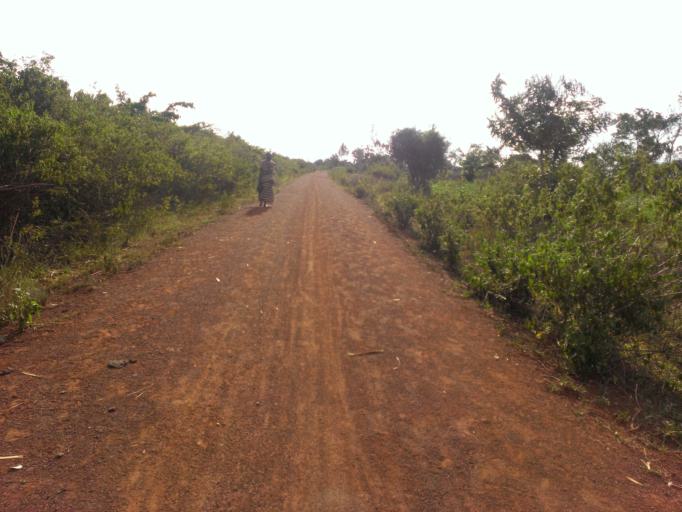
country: UG
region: Eastern Region
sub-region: Busia District
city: Busia
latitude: 0.5505
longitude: 33.9924
